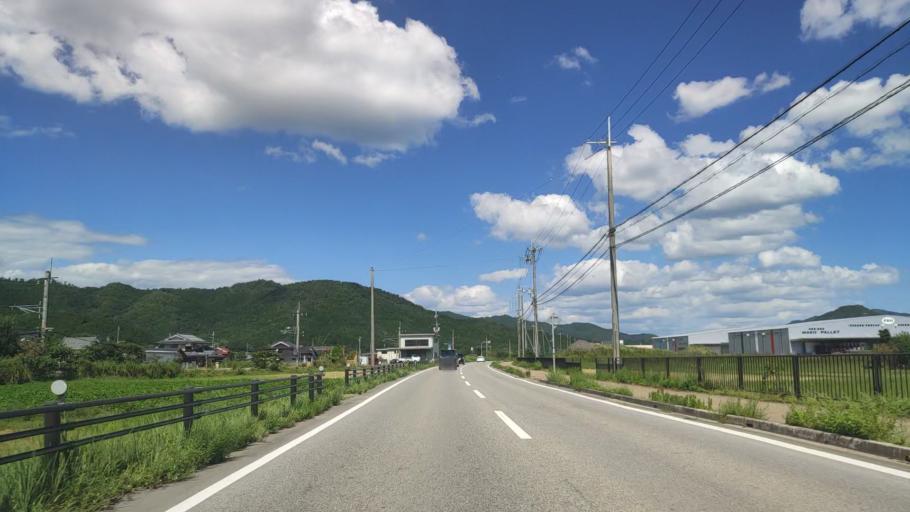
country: JP
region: Kyoto
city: Fukuchiyama
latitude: 35.1699
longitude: 135.1175
